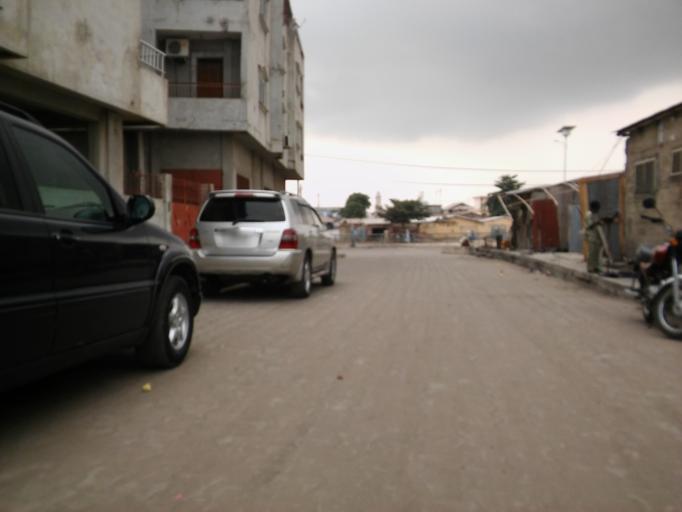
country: BJ
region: Littoral
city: Cotonou
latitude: 6.3825
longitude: 2.4229
